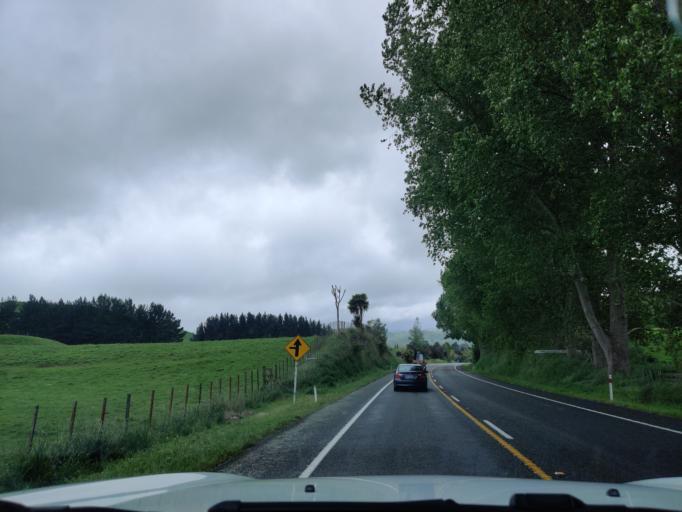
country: NZ
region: Manawatu-Wanganui
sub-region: Ruapehu District
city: Waiouru
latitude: -39.6484
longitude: 175.7683
